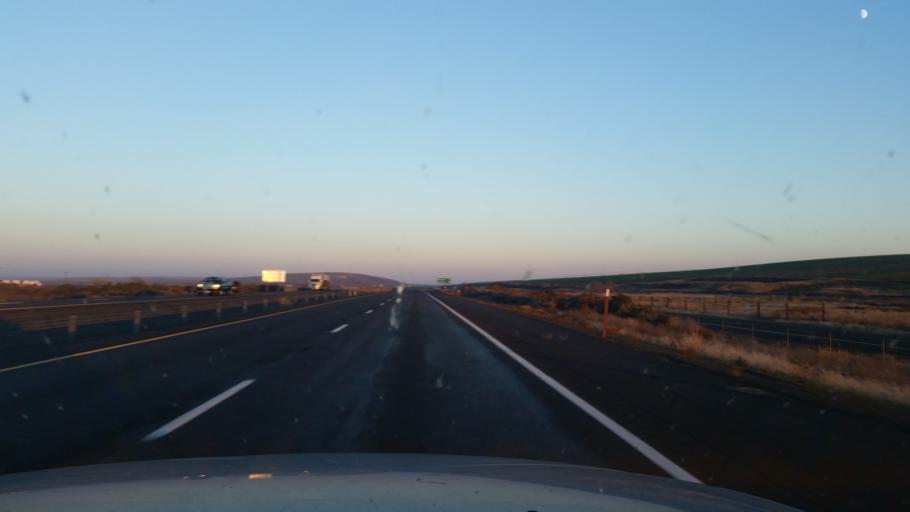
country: US
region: Washington
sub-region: Grant County
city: Warden
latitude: 47.0851
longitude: -119.0194
